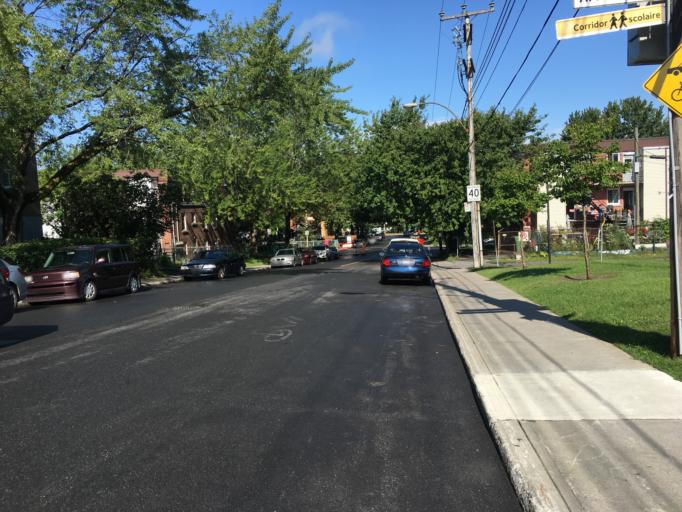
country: CA
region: Quebec
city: Mont-Royal
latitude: 45.5067
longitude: -73.6309
